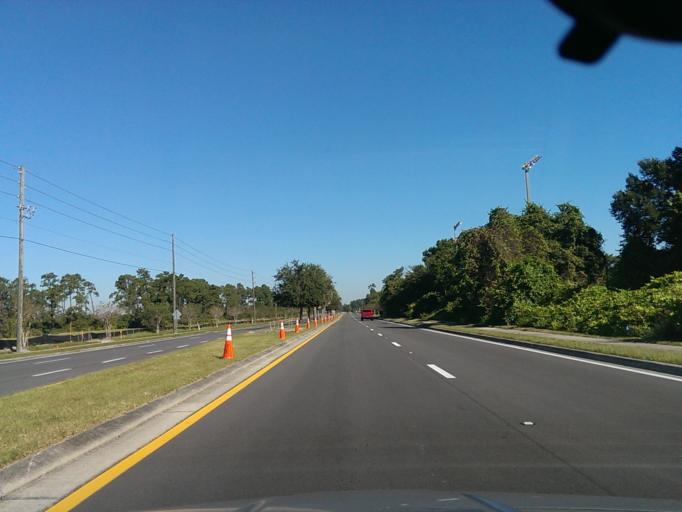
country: US
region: Florida
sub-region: Orange County
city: Doctor Phillips
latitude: 28.4099
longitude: -81.5327
